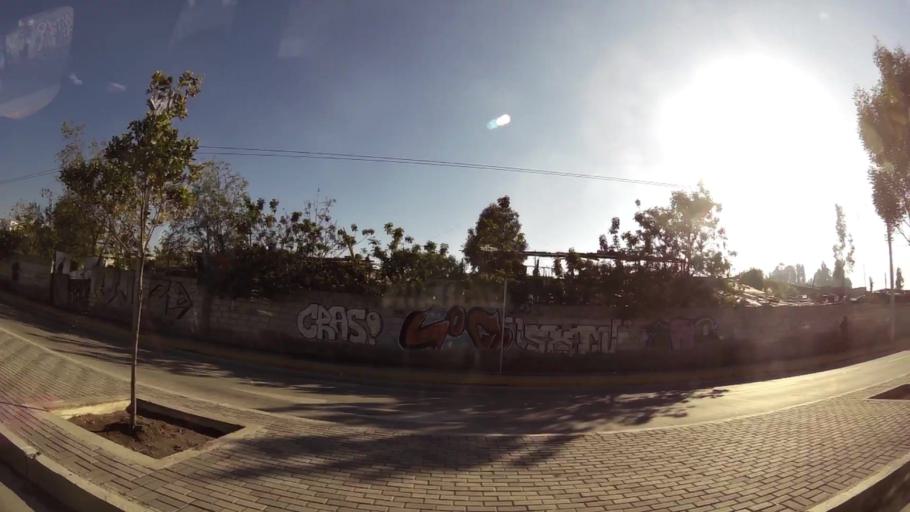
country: EC
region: Chimborazo
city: Riobamba
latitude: -1.6698
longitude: -78.6376
